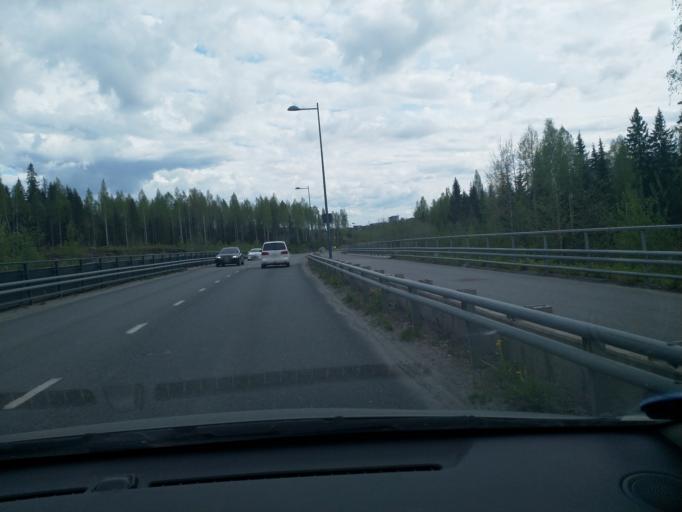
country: FI
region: Pirkanmaa
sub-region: Tampere
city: Tampere
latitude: 61.4481
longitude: 23.8062
